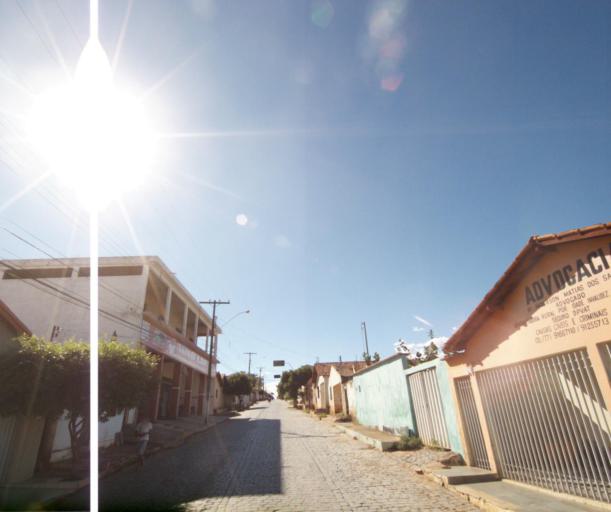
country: BR
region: Bahia
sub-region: Carinhanha
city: Carinhanha
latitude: -14.1816
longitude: -44.5379
